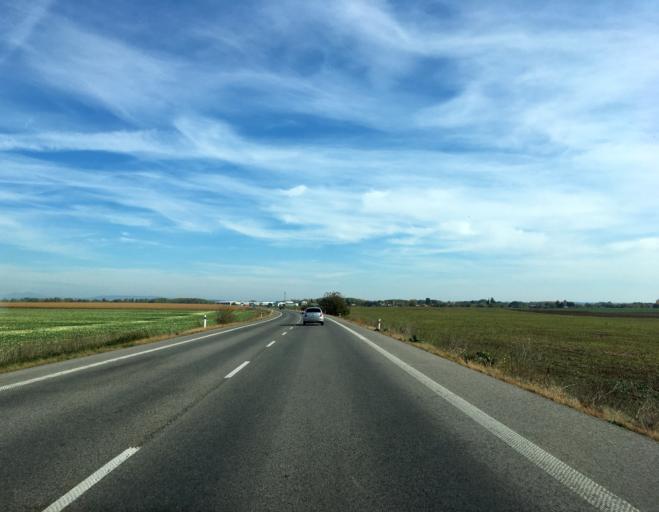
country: SK
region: Nitriansky
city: Zeliezovce
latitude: 48.1057
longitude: 18.6122
